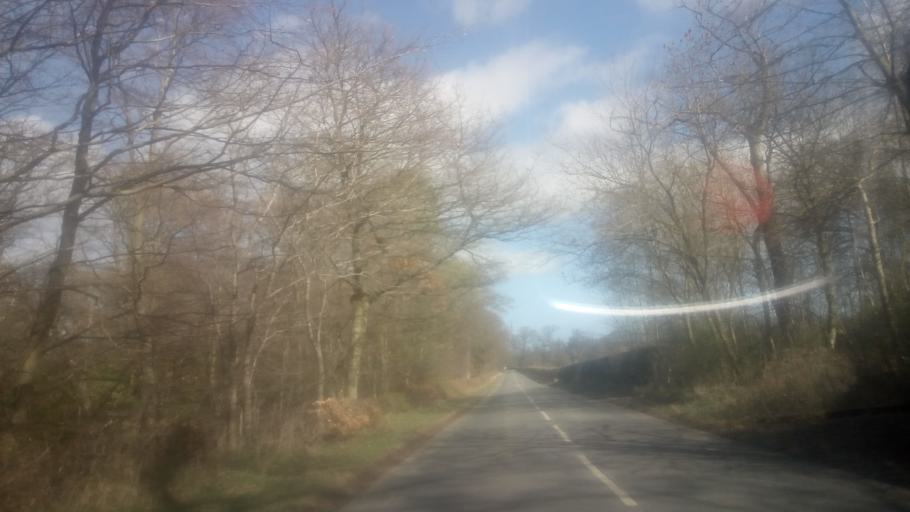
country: GB
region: Scotland
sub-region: Fife
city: Pathhead
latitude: 55.8880
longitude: -2.9594
